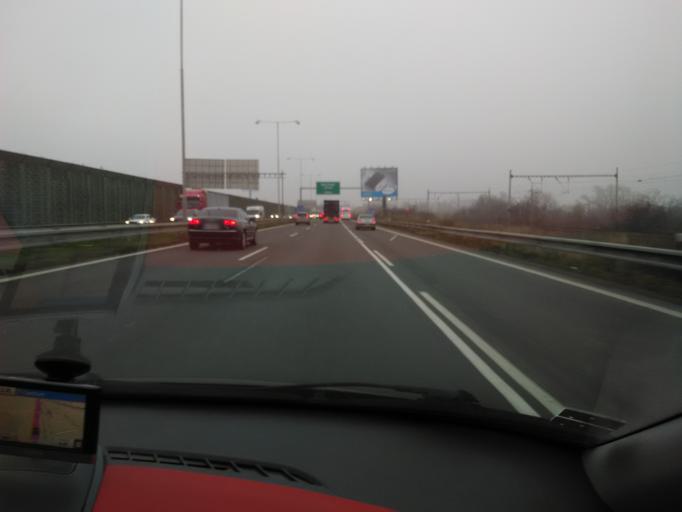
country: SK
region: Bratislavsky
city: Bratislava
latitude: 48.1420
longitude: 17.1591
